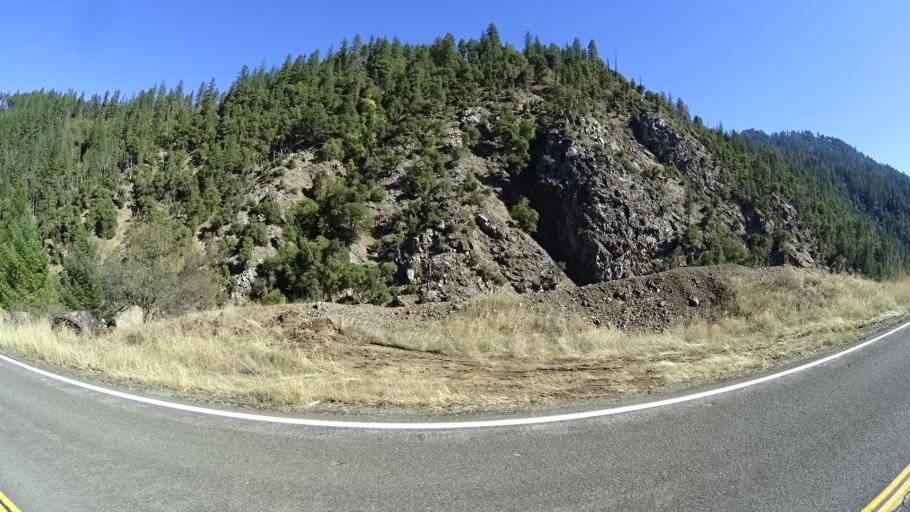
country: US
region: California
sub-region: Siskiyou County
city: Happy Camp
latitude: 41.3722
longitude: -123.4179
